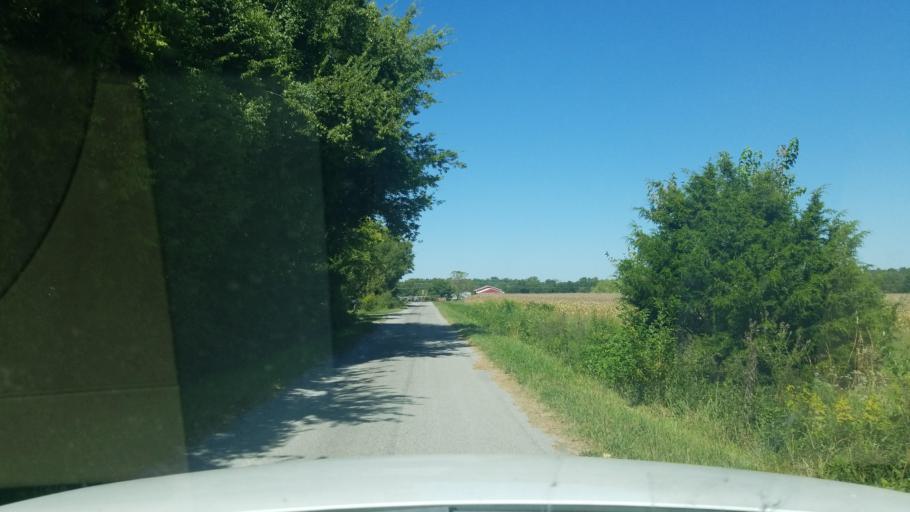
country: US
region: Illinois
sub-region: Saline County
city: Eldorado
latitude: 37.8598
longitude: -88.5119
